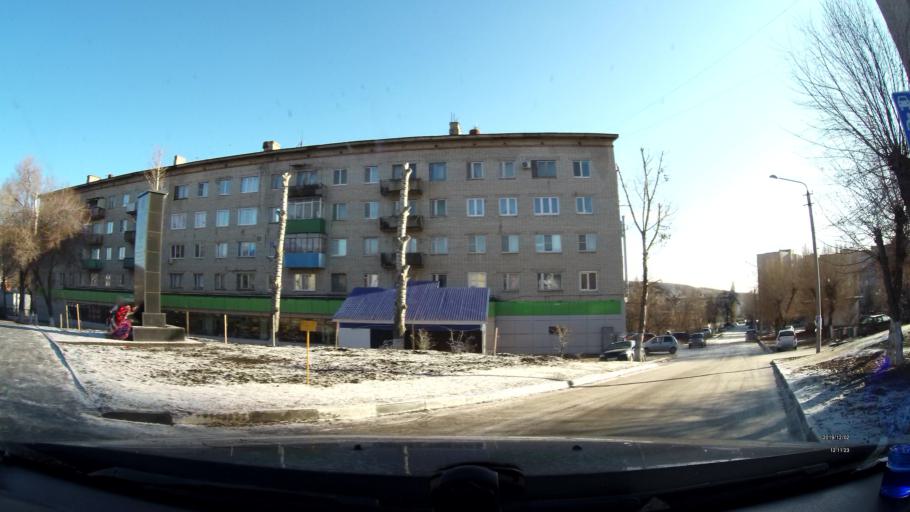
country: RU
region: Saratov
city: Vol'sk
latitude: 52.0537
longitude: 47.3831
